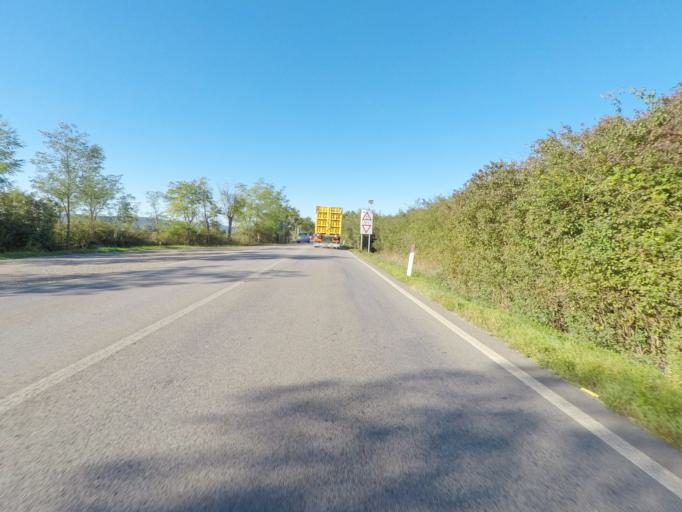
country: IT
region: Tuscany
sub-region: Provincia di Siena
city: Rosia
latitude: 43.2172
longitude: 11.2759
